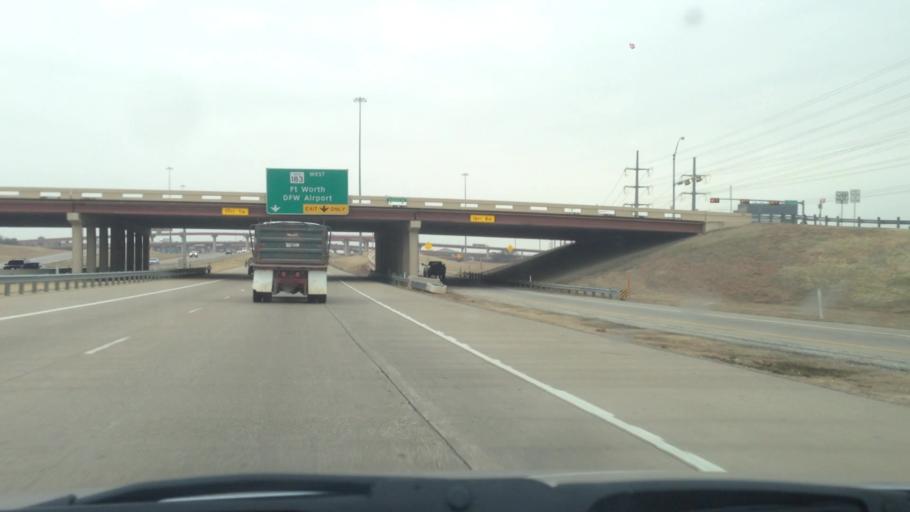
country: US
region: Texas
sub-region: Tarrant County
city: Euless
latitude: 32.8462
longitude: -97.0171
